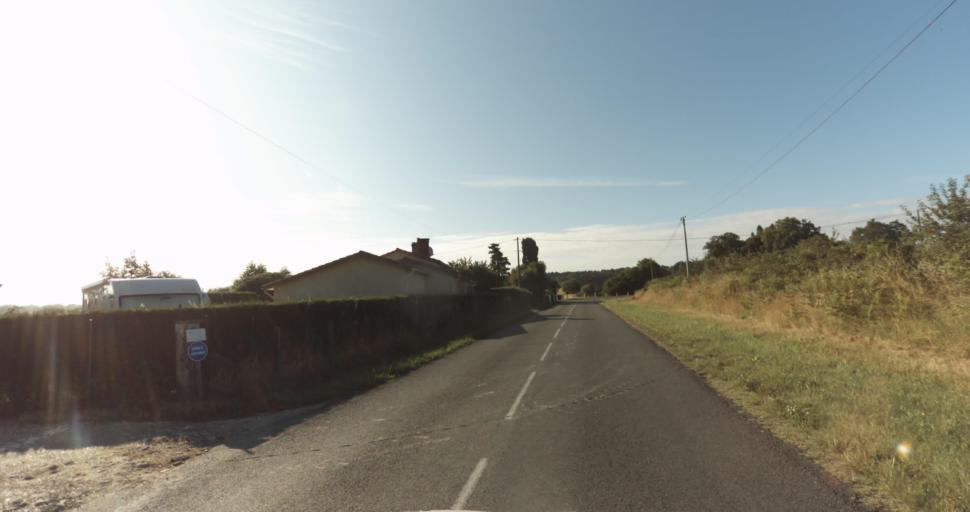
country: FR
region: Aquitaine
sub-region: Departement de la Gironde
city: Bazas
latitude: 44.4017
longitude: -0.2045
